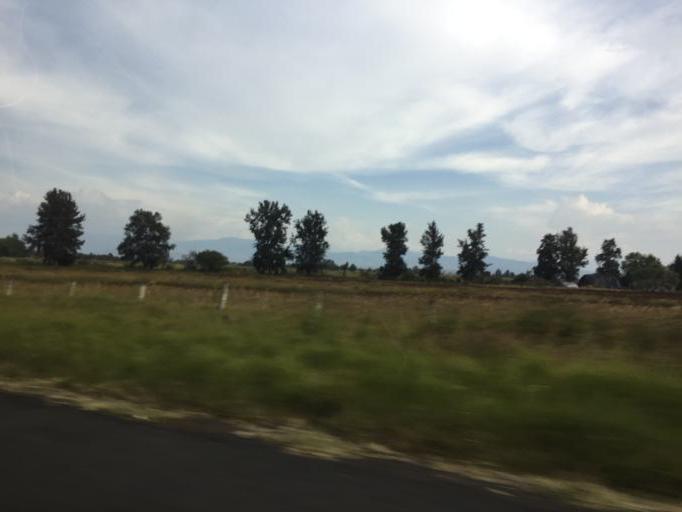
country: MX
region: Michoacan
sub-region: Alvaro Obregon
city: Lazaro Cardenas (La Purisima)
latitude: 19.8914
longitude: -101.0195
